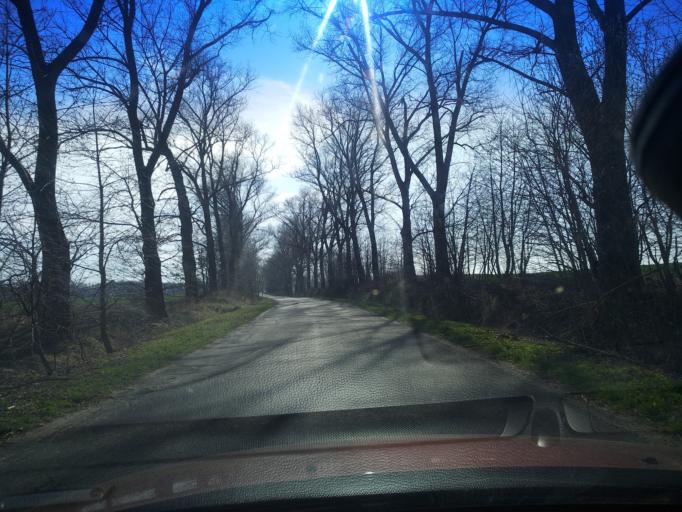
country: PL
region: Lower Silesian Voivodeship
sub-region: Powiat lubanski
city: Siekierczyn
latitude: 51.0578
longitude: 15.1518
